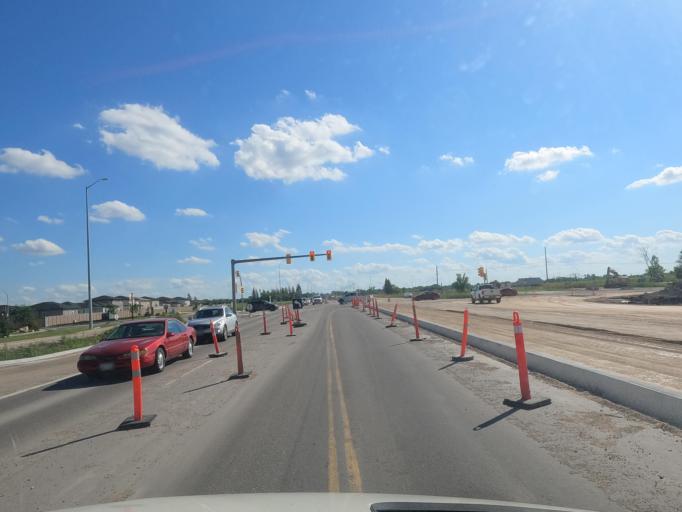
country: CA
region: Manitoba
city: Winnipeg
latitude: 49.9773
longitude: -97.0693
